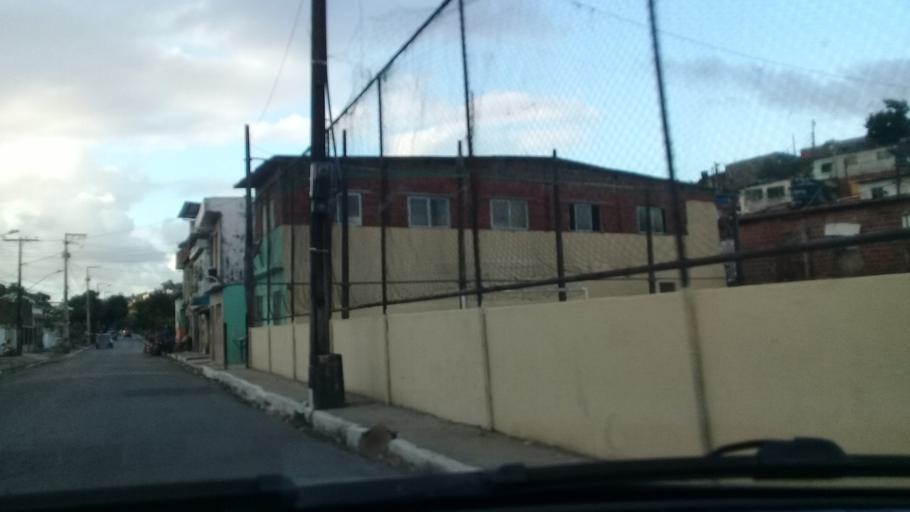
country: BR
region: Pernambuco
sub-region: Jaboatao Dos Guararapes
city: Jaboatao dos Guararapes
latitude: -8.1270
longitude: -34.9501
